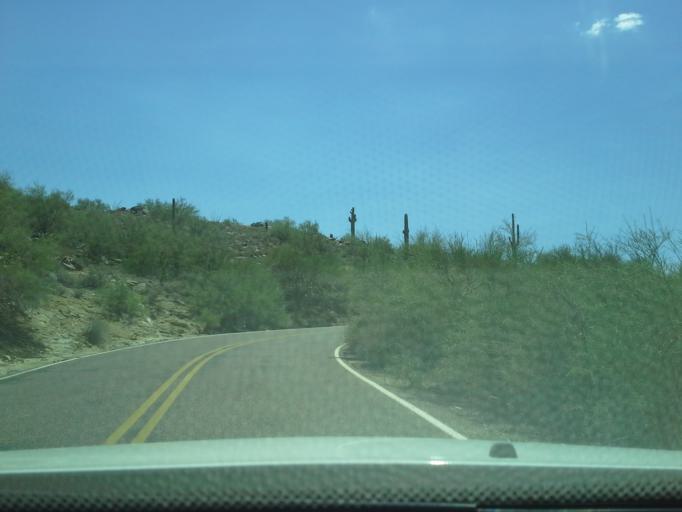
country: US
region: Arizona
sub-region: Maricopa County
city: Guadalupe
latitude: 33.3397
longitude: -112.0514
